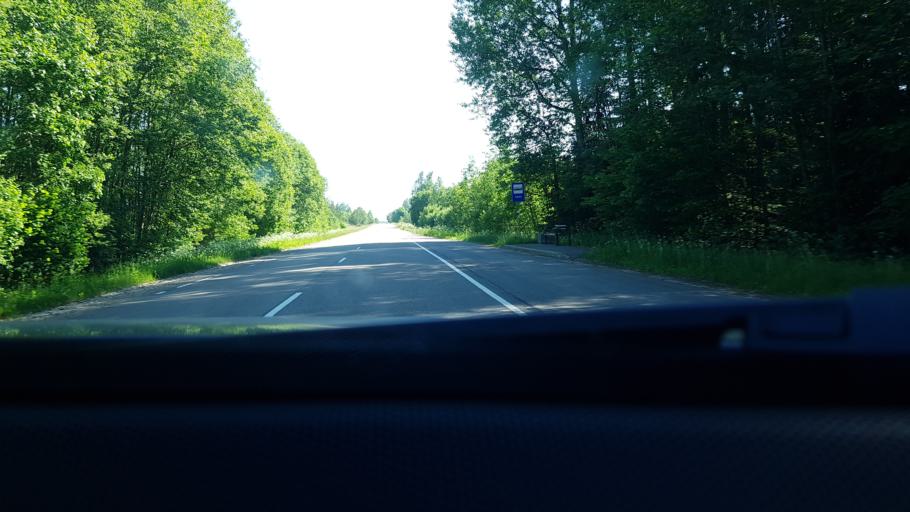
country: BY
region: Vitebsk
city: Braslaw
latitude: 55.8381
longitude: 26.9436
